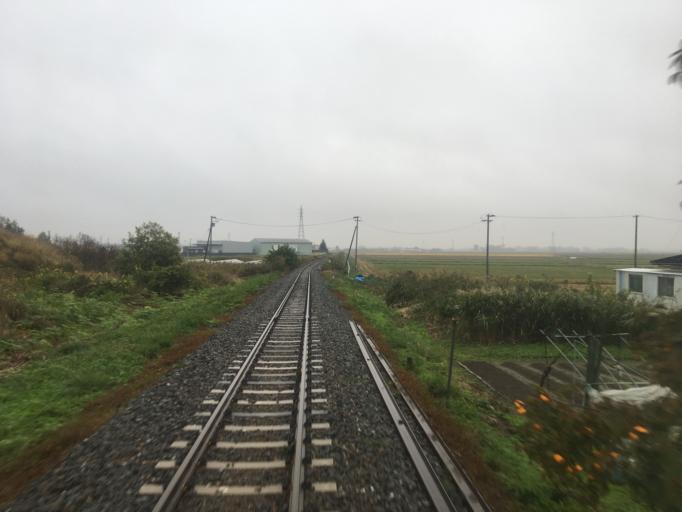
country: JP
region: Miyagi
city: Furukawa
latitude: 38.5683
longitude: 140.9853
